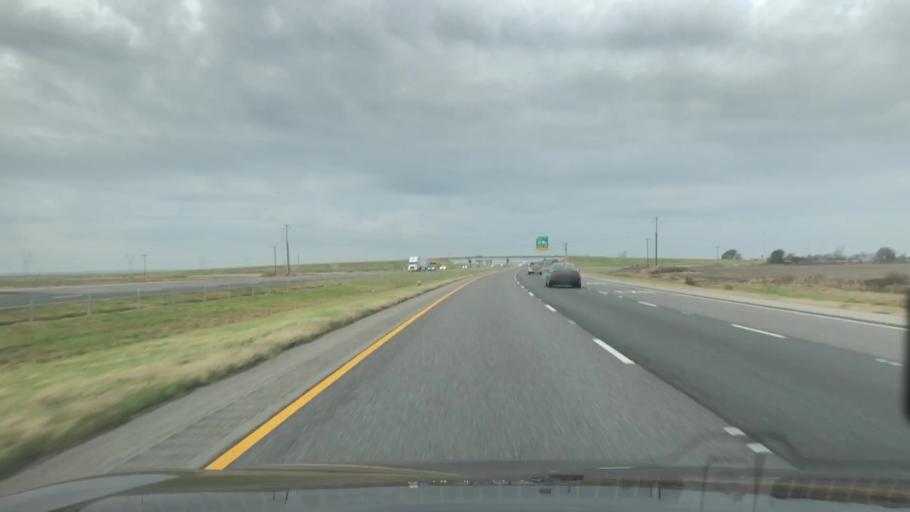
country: US
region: Mississippi
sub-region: Warren County
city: Vicksburg
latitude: 32.3203
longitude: -90.9555
